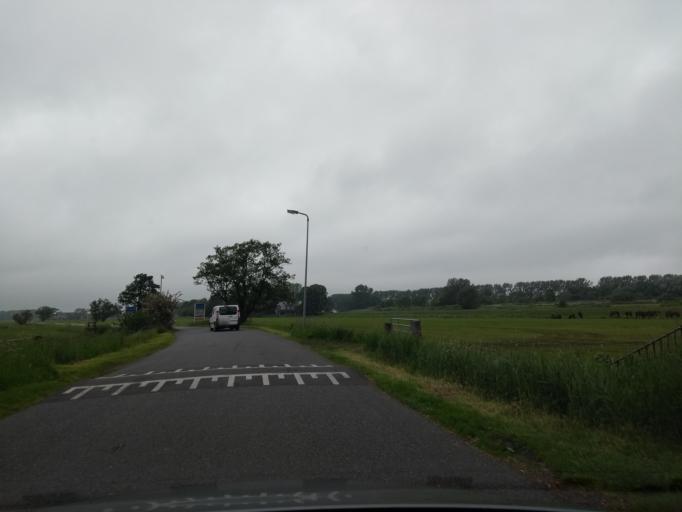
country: NL
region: Groningen
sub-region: Gemeente Zuidhorn
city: Aduard
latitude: 53.2511
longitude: 6.5132
